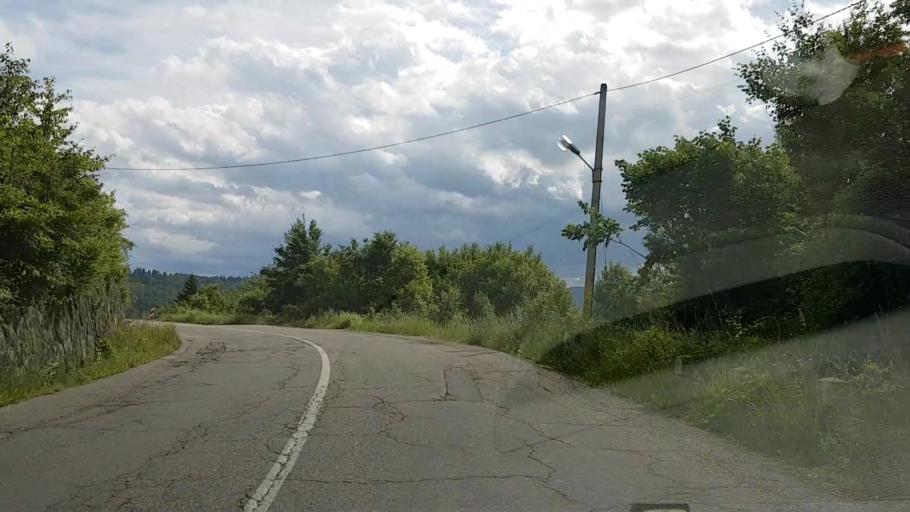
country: RO
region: Neamt
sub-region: Comuna Bicaz
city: Dodeni
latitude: 46.9938
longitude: 26.1008
